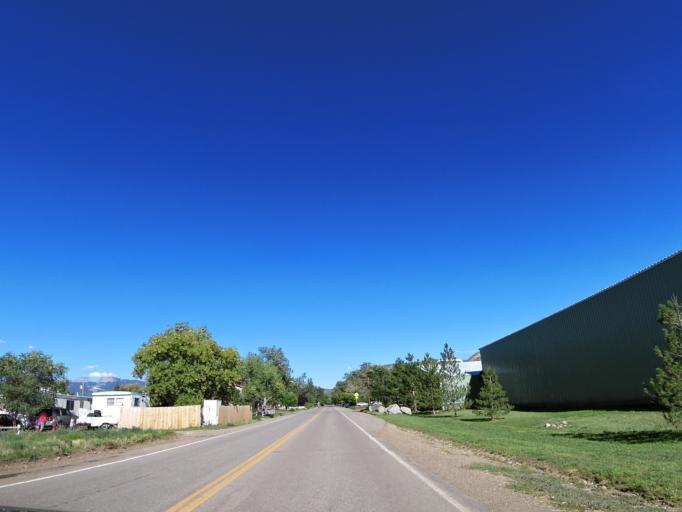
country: US
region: Colorado
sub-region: Montezuma County
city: Mancos
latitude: 37.3449
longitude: -108.3035
